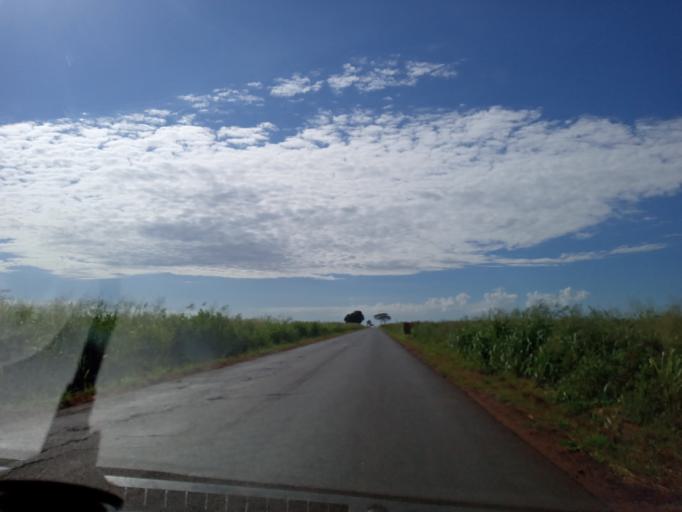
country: BR
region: Goias
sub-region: Itumbiara
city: Itumbiara
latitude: -18.4494
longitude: -49.1636
